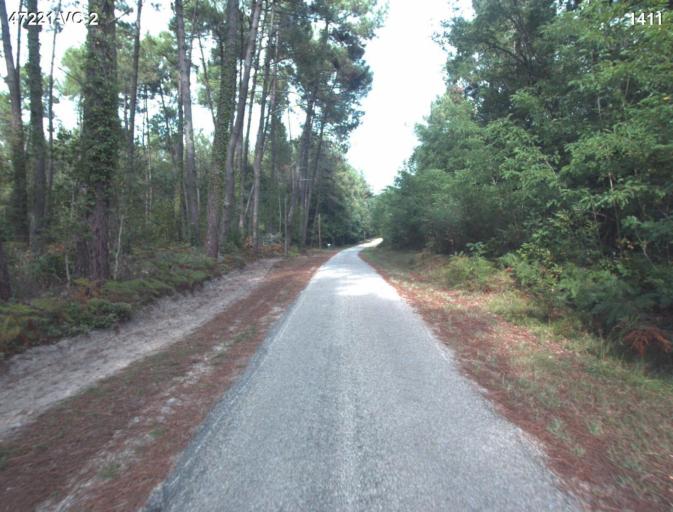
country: FR
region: Aquitaine
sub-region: Departement du Lot-et-Garonne
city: Mezin
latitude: 44.1018
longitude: 0.2286
